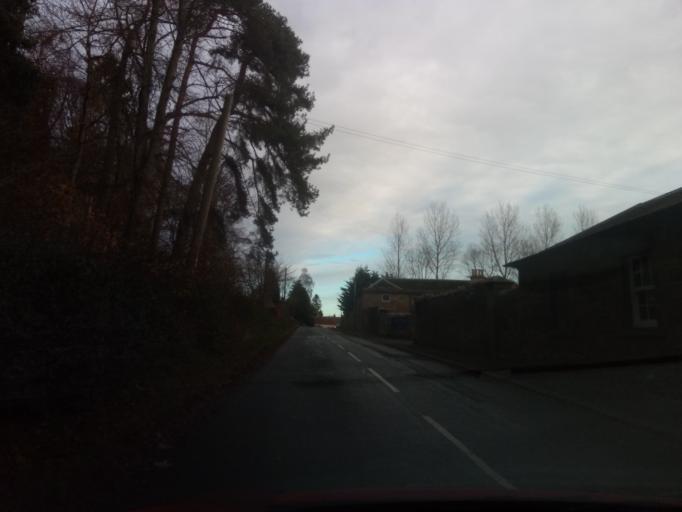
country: GB
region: Scotland
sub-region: The Scottish Borders
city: Coldstream
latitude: 55.6604
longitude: -2.2387
